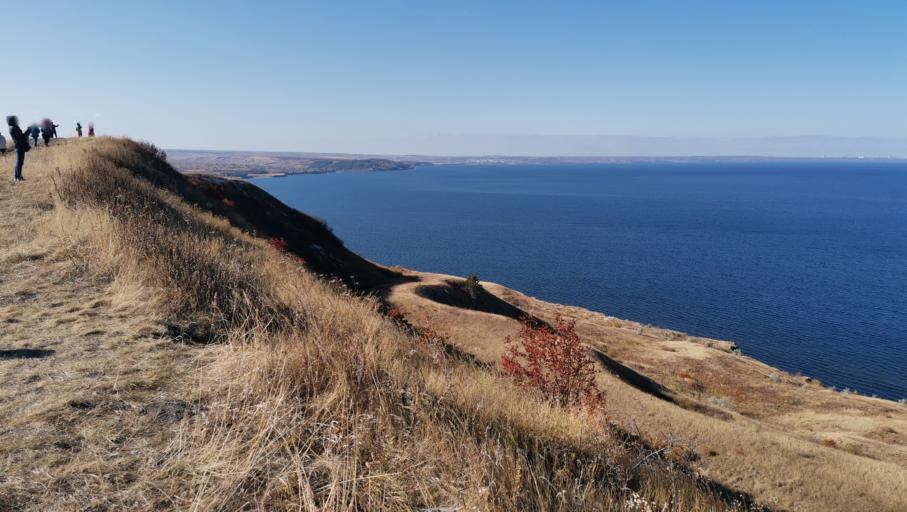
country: RU
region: Ulyanovsk
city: Novoul'yanovsk
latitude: 54.1140
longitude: 48.5739
